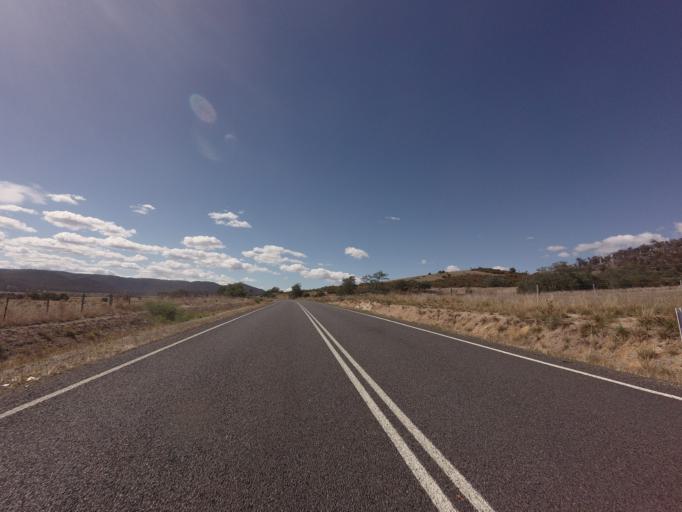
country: AU
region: Tasmania
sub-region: Break O'Day
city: St Helens
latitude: -41.6977
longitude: 147.8615
